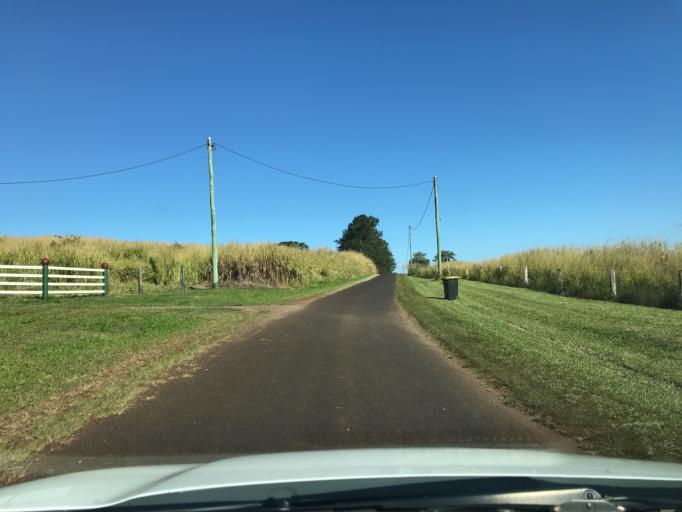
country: AU
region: Queensland
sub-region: Tablelands
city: Atherton
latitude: -17.2915
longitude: 145.5447
